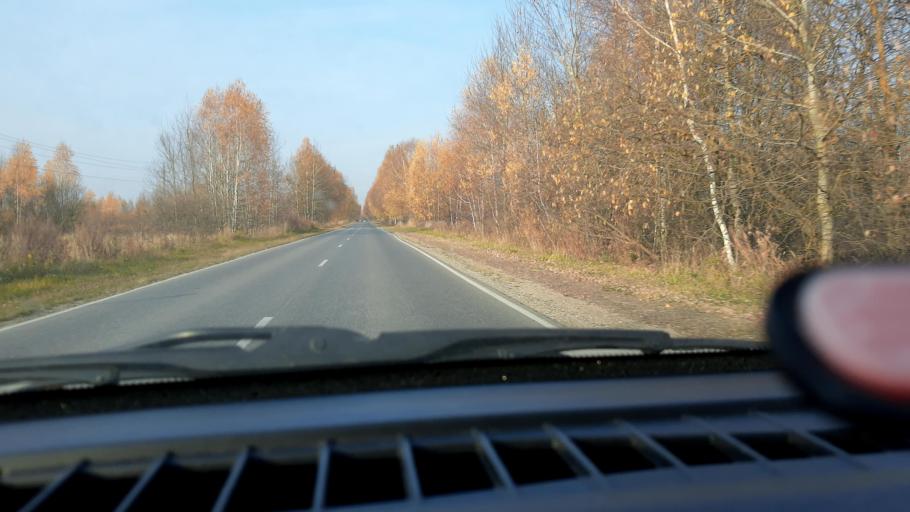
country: RU
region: Nizjnij Novgorod
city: Neklyudovo
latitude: 56.5110
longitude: 43.8402
